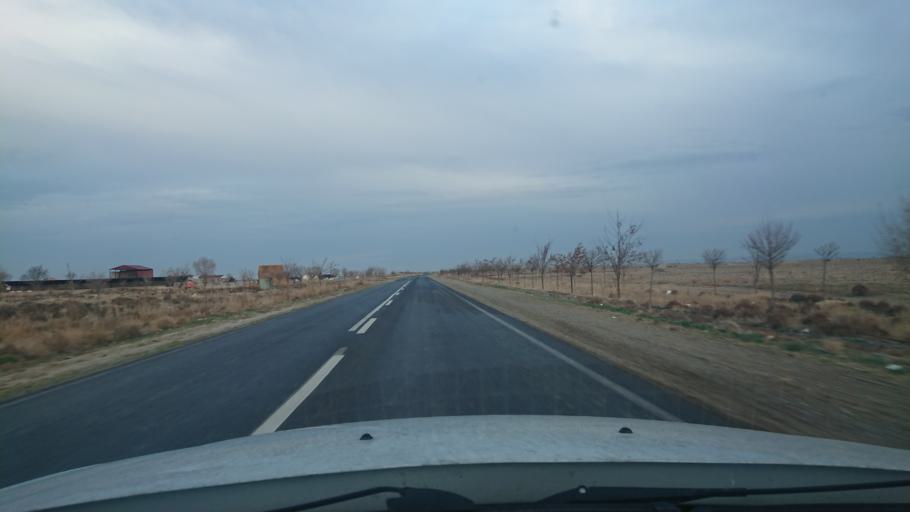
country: TR
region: Aksaray
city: Yesilova
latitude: 38.3049
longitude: 33.7558
